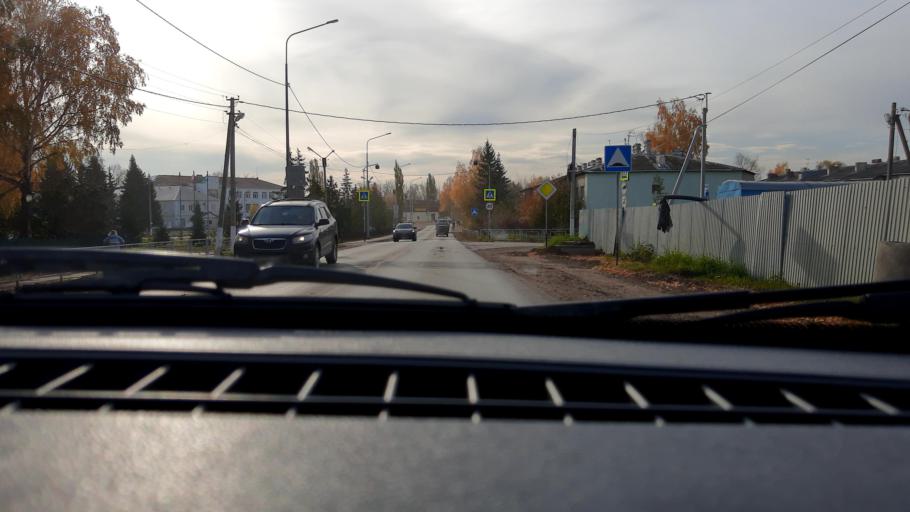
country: RU
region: Bashkortostan
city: Mikhaylovka
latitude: 54.8049
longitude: 55.8911
